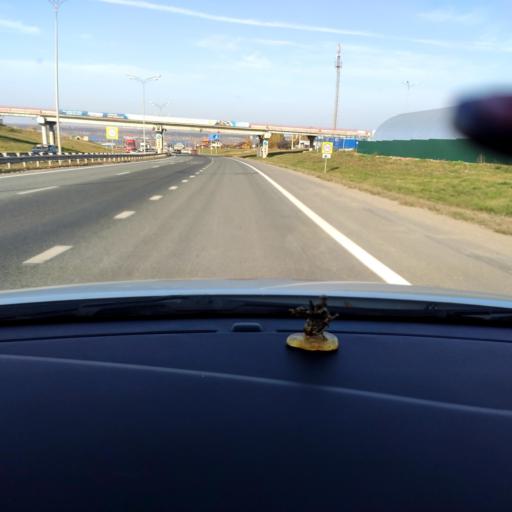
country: RU
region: Tatarstan
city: Osinovo
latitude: 55.7724
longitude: 48.8381
